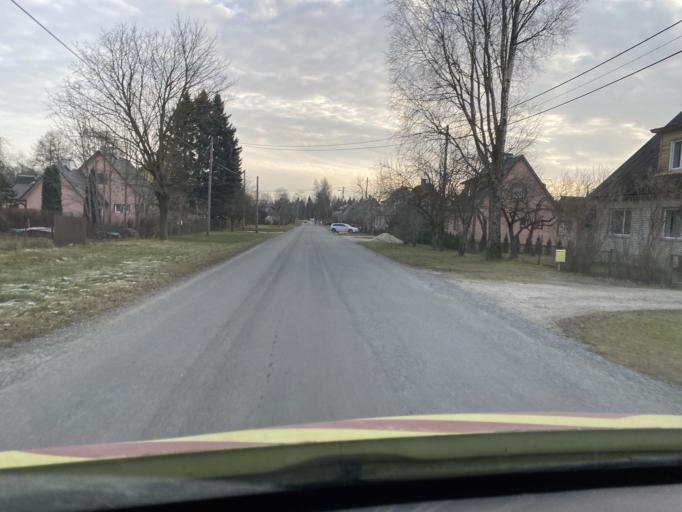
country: EE
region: Jogevamaa
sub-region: Poltsamaa linn
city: Poltsamaa
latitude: 58.6457
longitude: 25.9720
